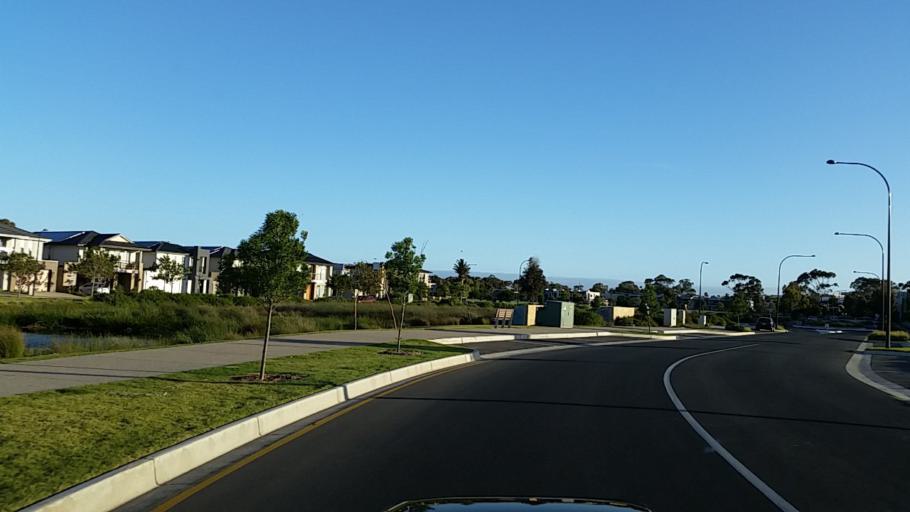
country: AU
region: South Australia
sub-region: Charles Sturt
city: Woodville North
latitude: -34.8704
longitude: 138.5343
